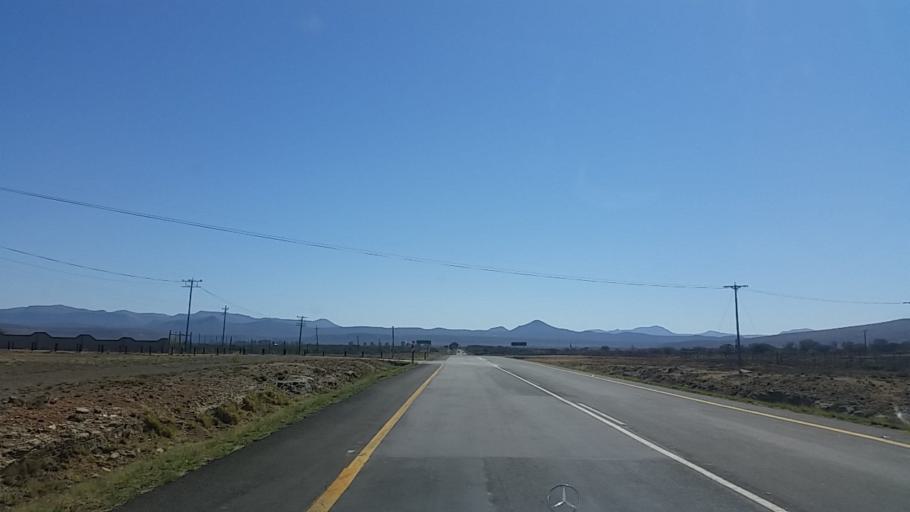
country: ZA
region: Eastern Cape
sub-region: Cacadu District Municipality
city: Graaff-Reinet
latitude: -32.2210
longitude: 24.5414
